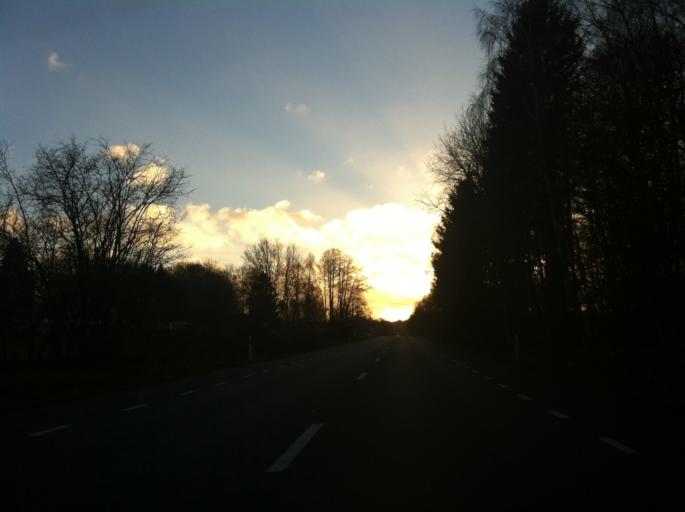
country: SE
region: Skane
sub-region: Hassleholms Kommun
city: Sosdala
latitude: 56.0420
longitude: 13.7031
